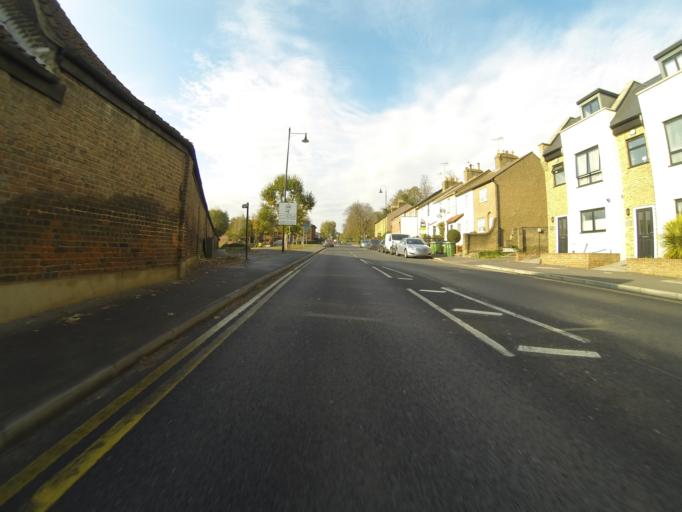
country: GB
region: England
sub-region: Greater London
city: Bexley
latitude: 51.4519
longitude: 0.1738
